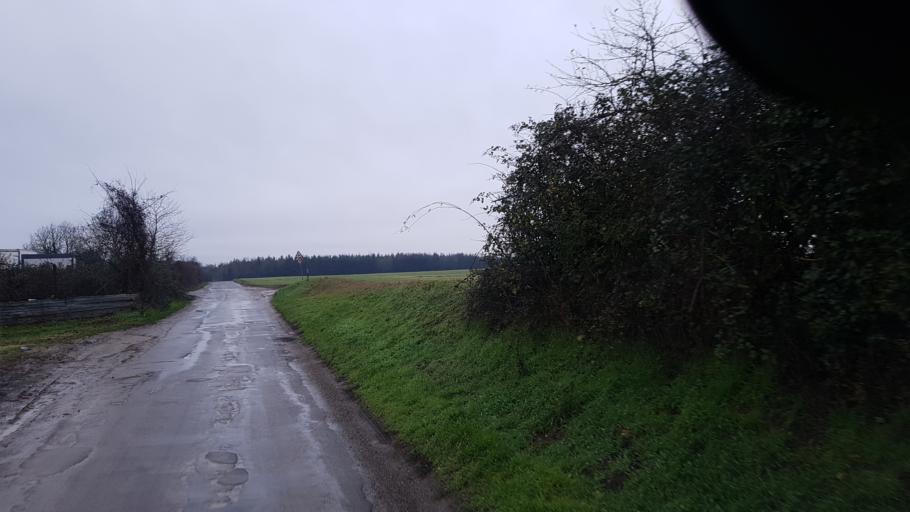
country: FR
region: Ile-de-France
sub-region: Departement de l'Essonne
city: Etampes
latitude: 48.4168
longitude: 2.1409
